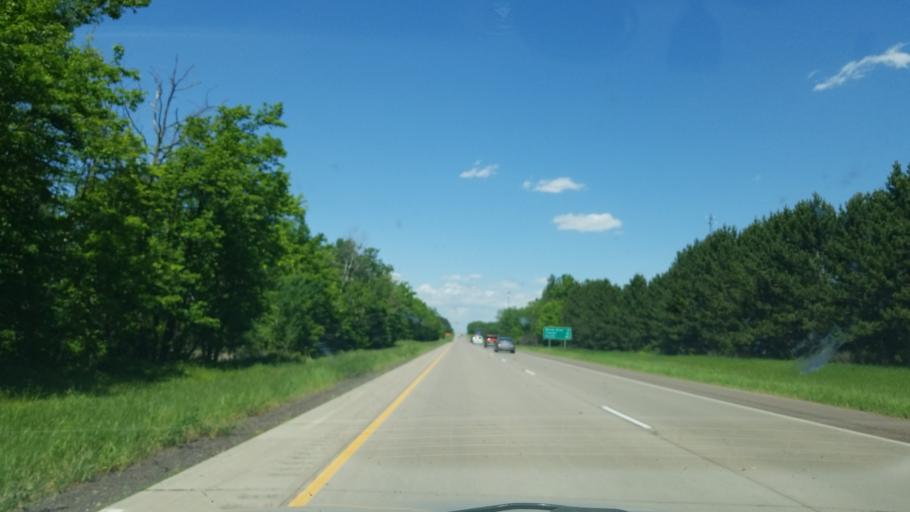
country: US
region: Minnesota
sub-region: Pine County
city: Sandstone
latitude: 46.1895
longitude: -92.8508
